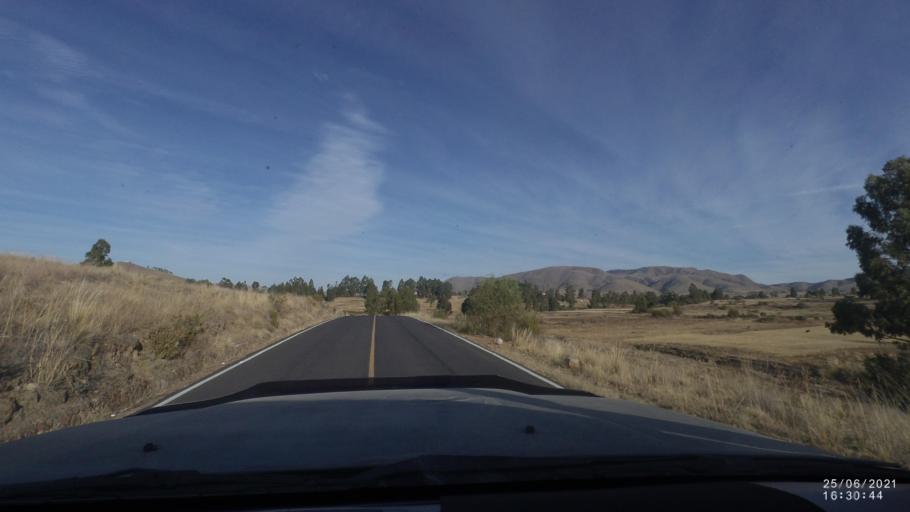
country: BO
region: Cochabamba
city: Arani
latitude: -17.7953
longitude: -65.8040
